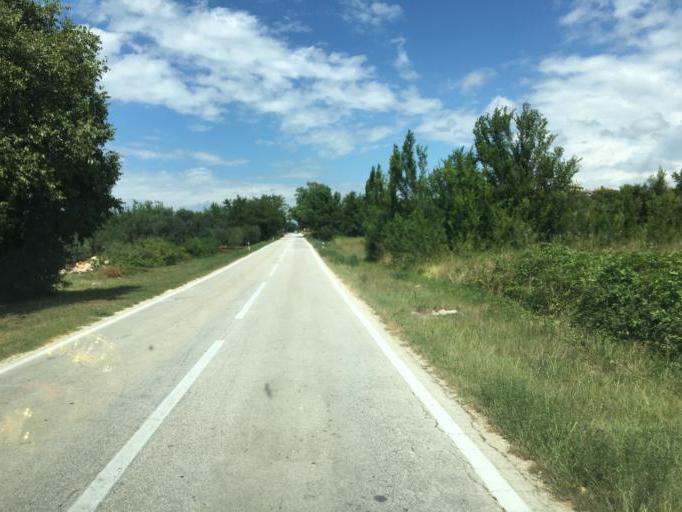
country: HR
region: Istarska
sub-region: Grad Rovinj
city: Rovinj
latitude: 45.1717
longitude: 13.7419
